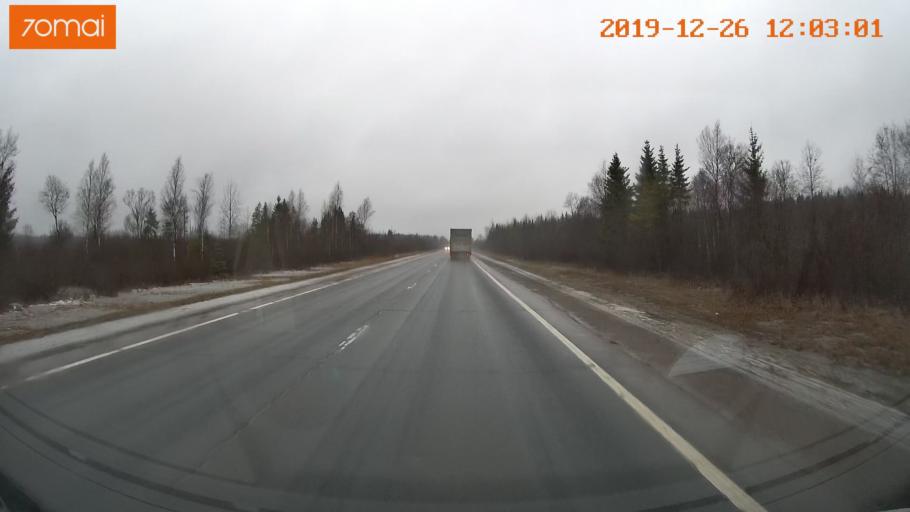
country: RU
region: Vologda
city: Tonshalovo
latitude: 59.3038
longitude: 38.1339
